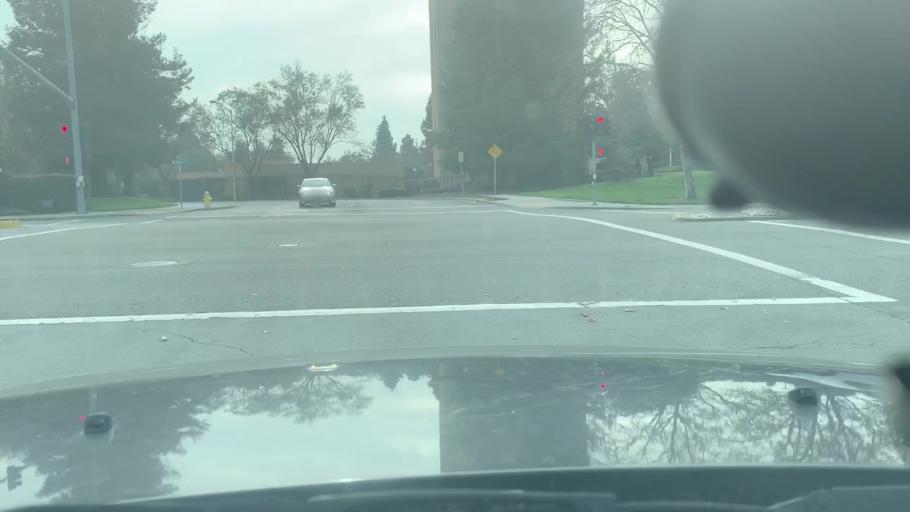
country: US
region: California
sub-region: Alameda County
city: Newark
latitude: 37.5361
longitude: -122.0287
